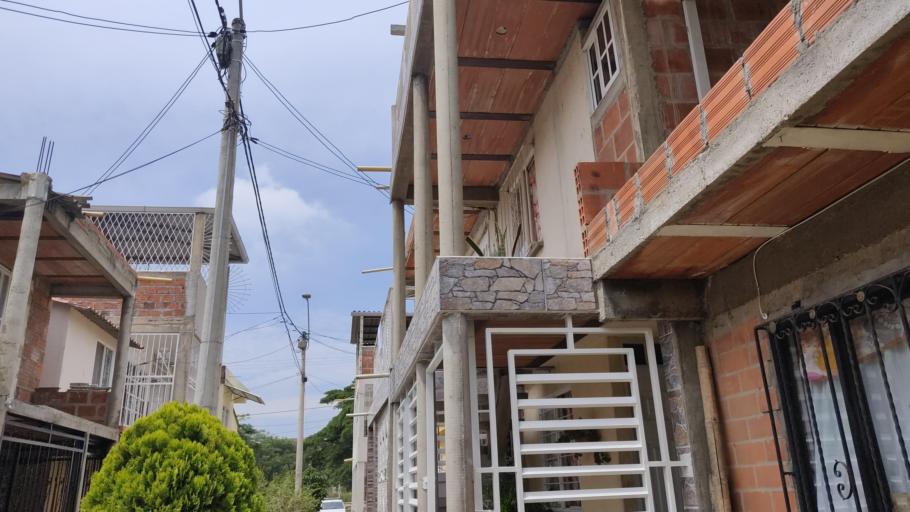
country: CO
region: Valle del Cauca
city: Jamundi
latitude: 3.2354
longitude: -76.5132
